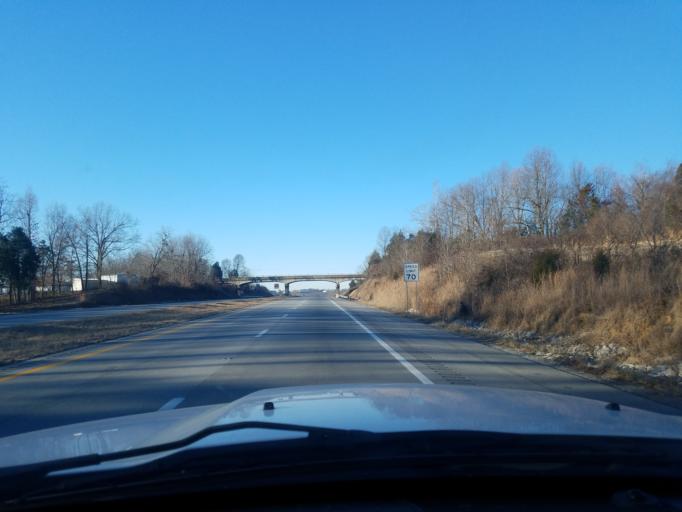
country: US
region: Kentucky
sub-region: Grayson County
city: Leitchfield
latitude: 37.4600
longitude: -86.3081
